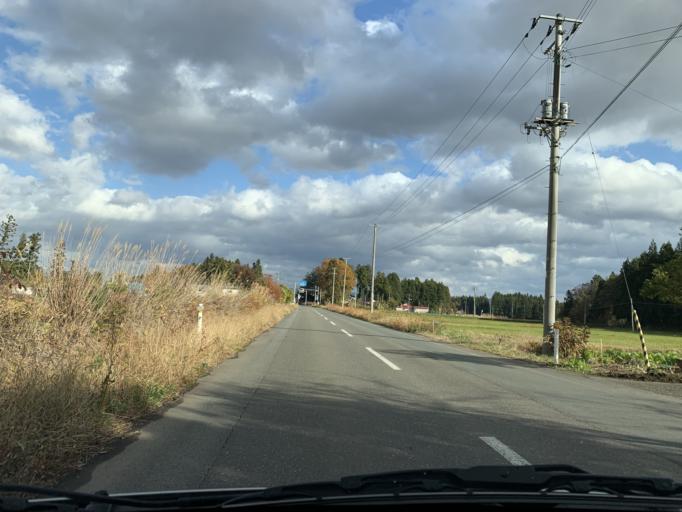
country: JP
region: Iwate
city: Mizusawa
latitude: 39.1191
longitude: 141.0506
